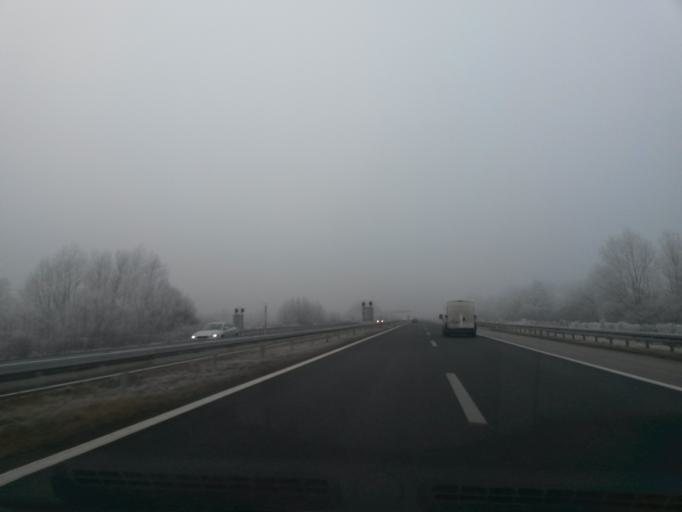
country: HR
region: Zagrebacka
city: Brckovljani
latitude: 45.9280
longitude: 16.2716
